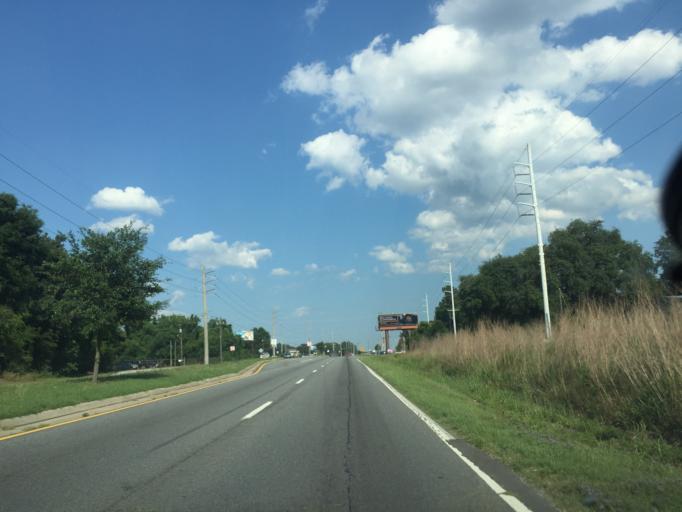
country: US
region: Georgia
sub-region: Chatham County
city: Thunderbolt
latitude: 32.0706
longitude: -81.0605
